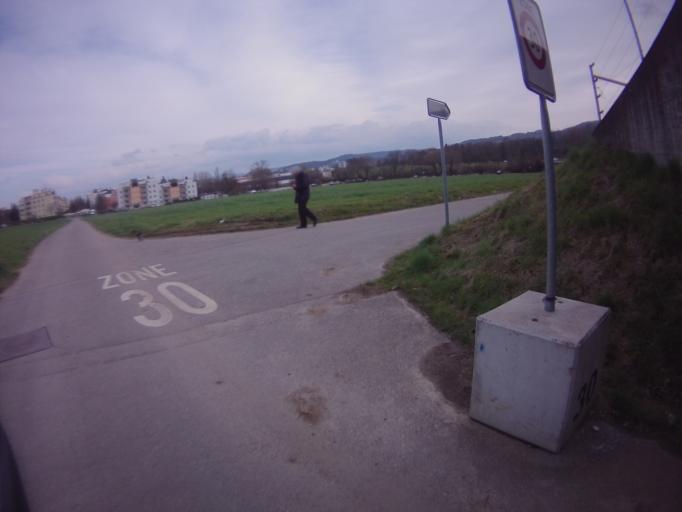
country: CH
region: Zurich
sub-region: Bezirk Dietikon
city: Dietikon / Vorstadt
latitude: 47.4301
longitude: 8.3887
